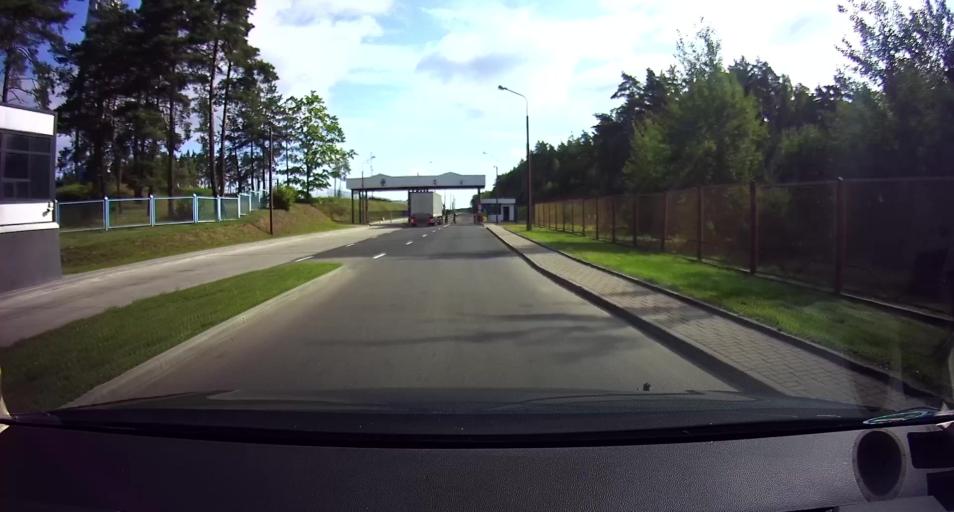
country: PL
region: Podlasie
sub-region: Powiat sokolski
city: Kuznica
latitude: 53.5240
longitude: 23.6699
